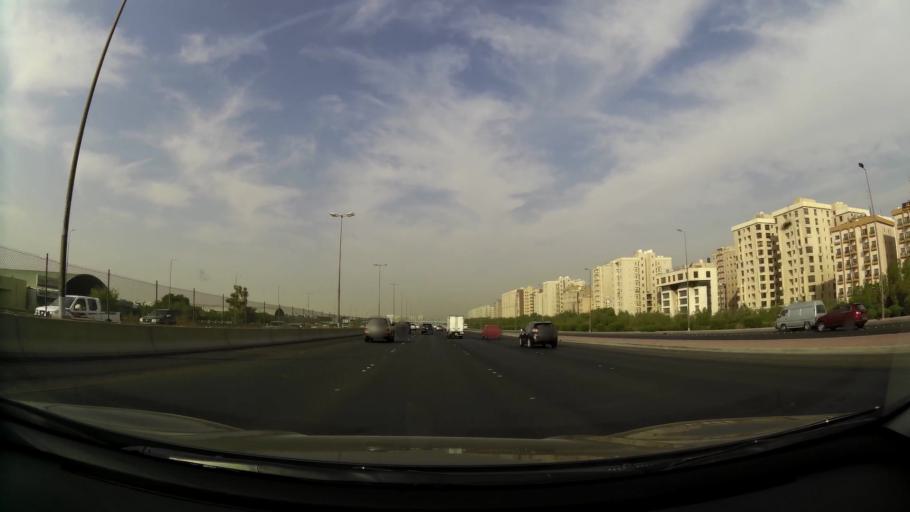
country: KW
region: Al Farwaniyah
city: Janub as Surrah
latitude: 29.2658
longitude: 47.9674
